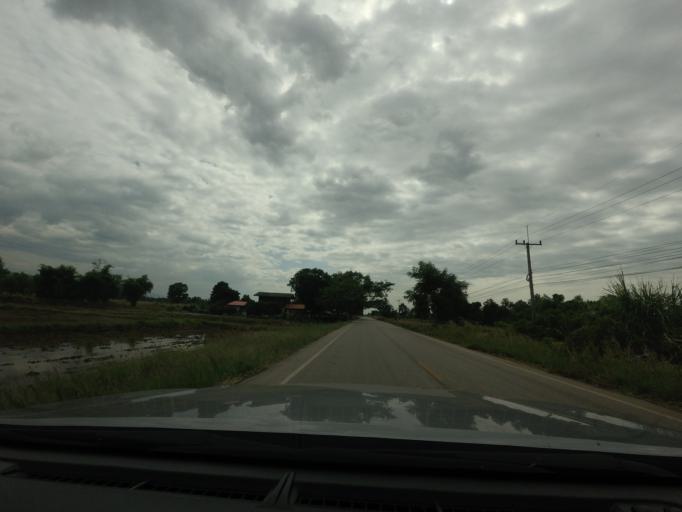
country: TH
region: Phitsanulok
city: Noen Maprang
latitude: 16.6520
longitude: 100.6161
